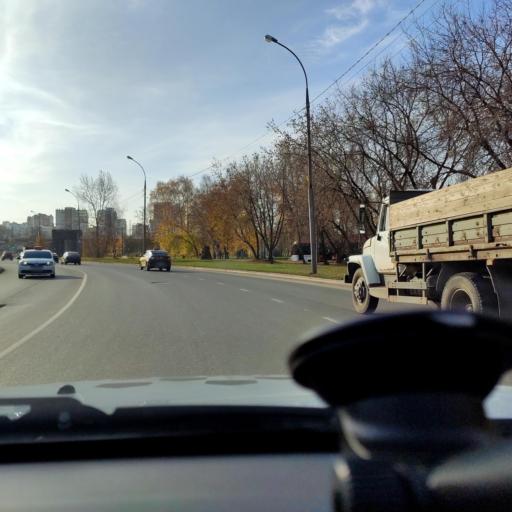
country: RU
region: Perm
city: Perm
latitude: 58.0068
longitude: 56.1931
